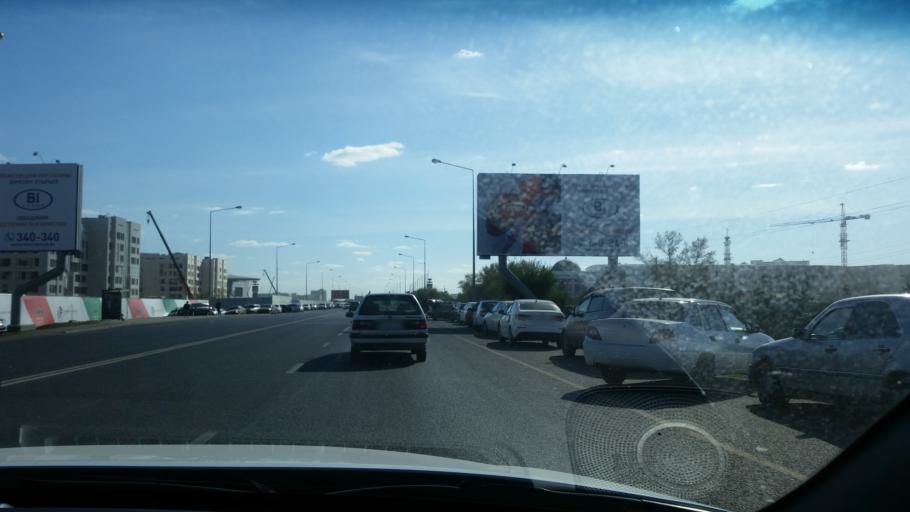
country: KZ
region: Astana Qalasy
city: Astana
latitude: 51.0946
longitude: 71.4044
